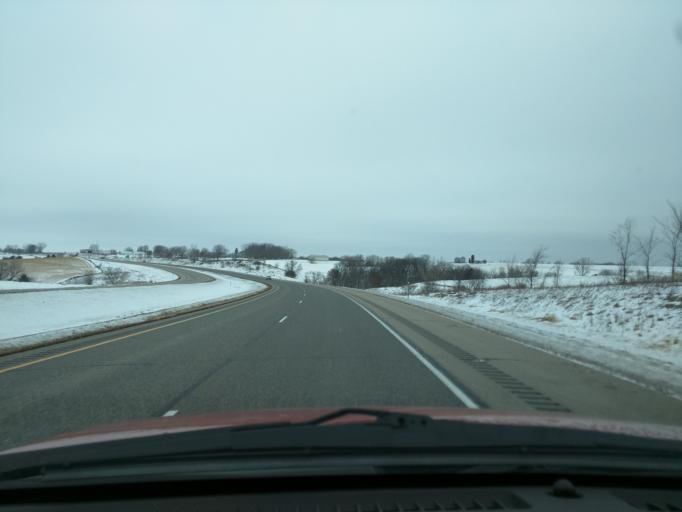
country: US
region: Minnesota
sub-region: Winona County
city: Winona
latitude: 43.9549
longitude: -91.6551
